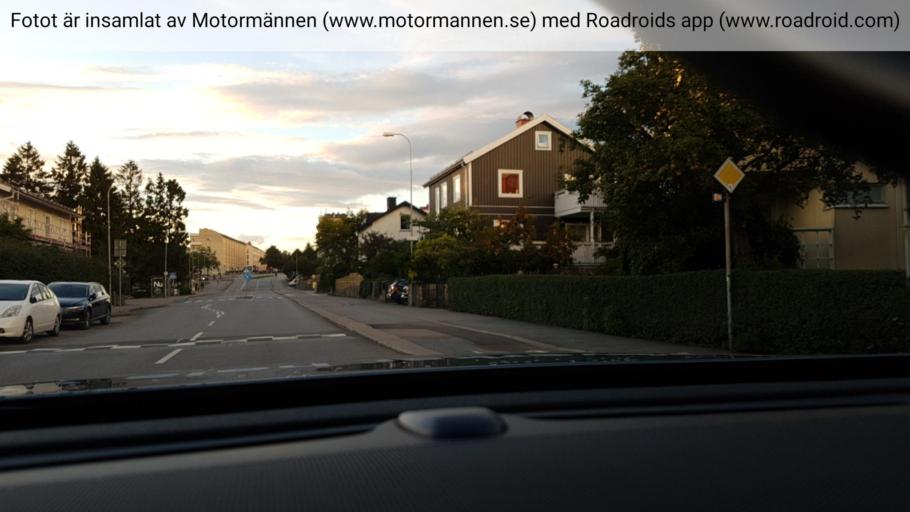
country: SE
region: Vaestra Goetaland
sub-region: Goteborg
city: Goeteborg
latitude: 57.6838
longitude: 11.9861
